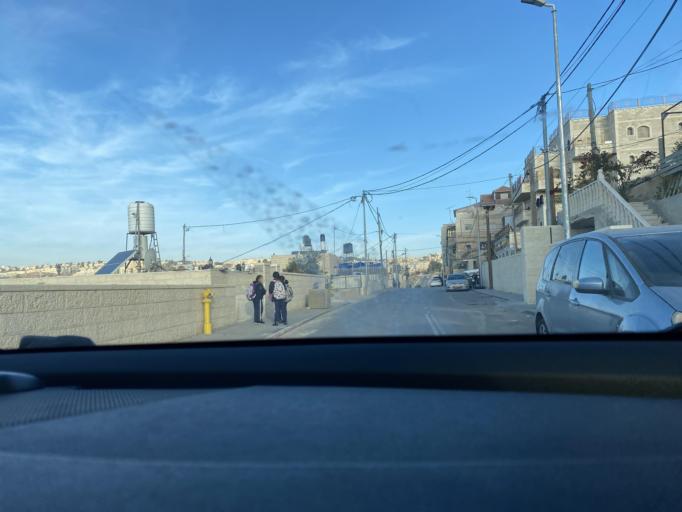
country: PS
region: West Bank
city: Ash Shaykh Sa`d
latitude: 31.7389
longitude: 35.2428
